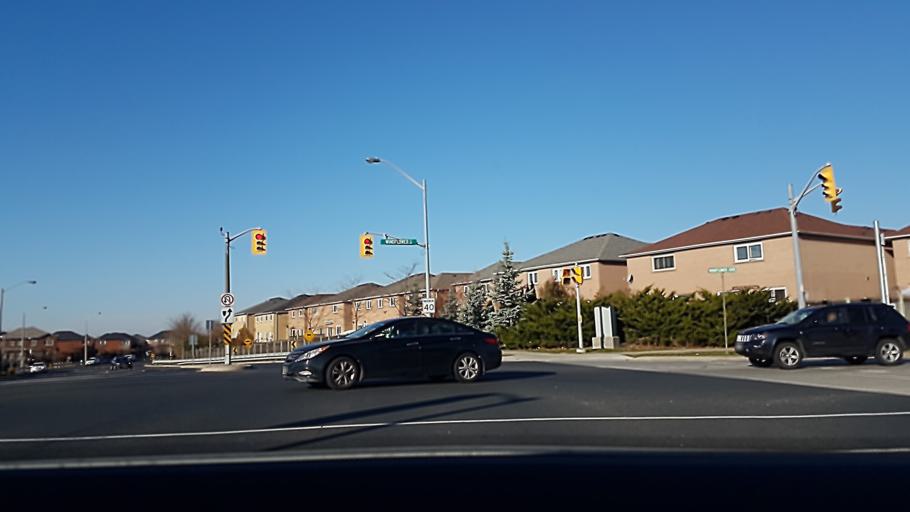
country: CA
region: Ontario
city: Concord
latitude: 43.7890
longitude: -79.5574
